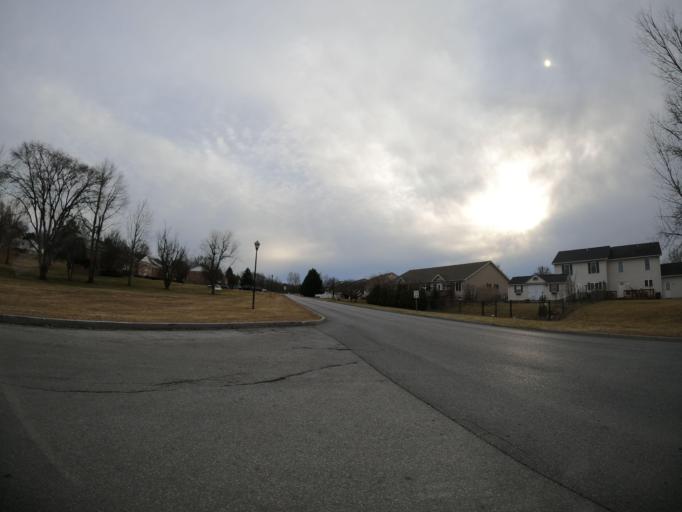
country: US
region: West Virginia
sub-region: Jefferson County
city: Ranson
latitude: 39.2949
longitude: -77.8980
